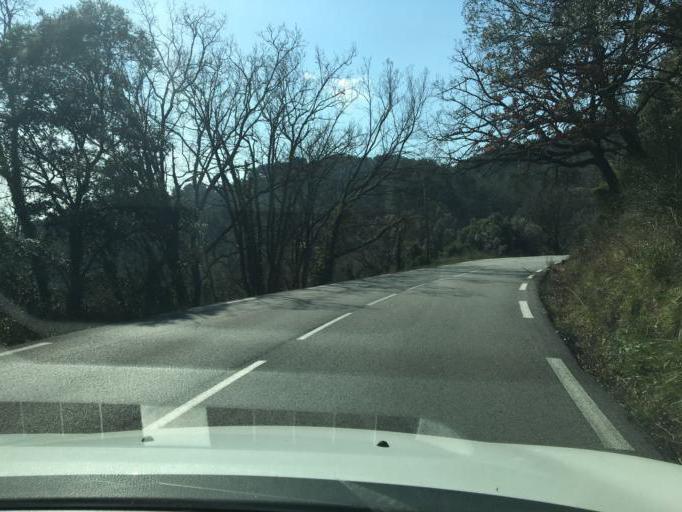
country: FR
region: Provence-Alpes-Cote d'Azur
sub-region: Departement du Var
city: Bargemon
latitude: 43.6060
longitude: 6.5517
